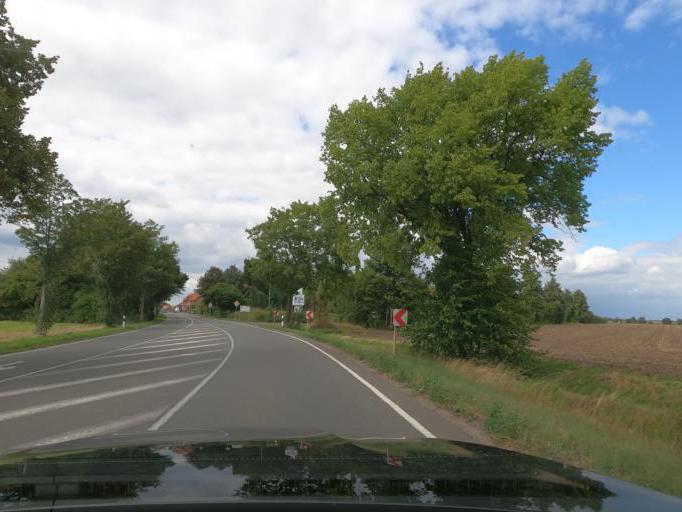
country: DE
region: Lower Saxony
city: Algermissen
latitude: 52.2518
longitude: 9.9834
